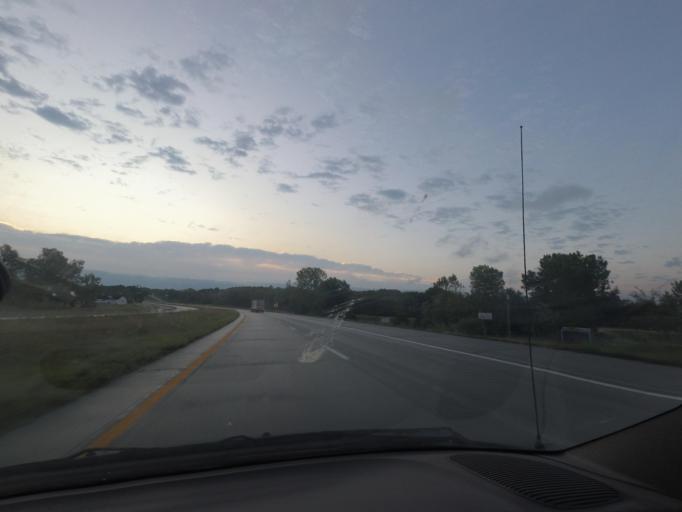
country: US
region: Missouri
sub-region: Macon County
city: Macon
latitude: 39.7469
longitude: -92.4979
